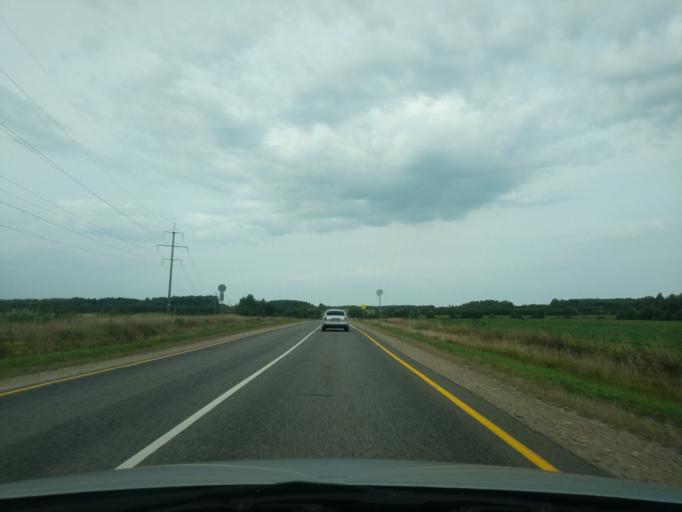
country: RU
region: Kirov
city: Mirnyy
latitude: 58.2725
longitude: 47.7913
